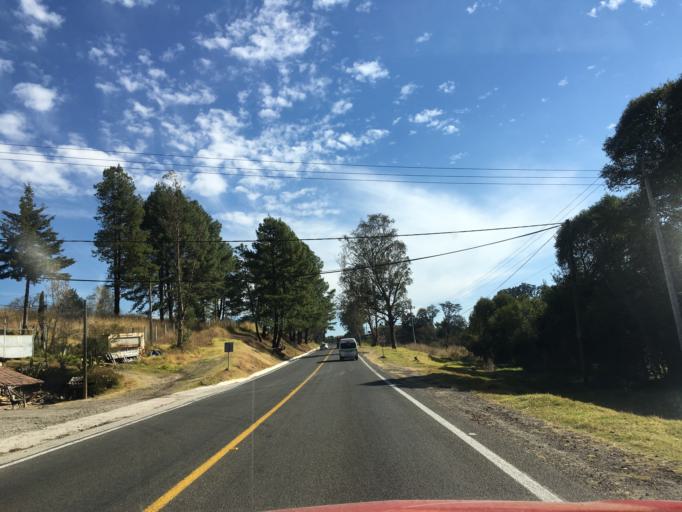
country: MX
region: Michoacan
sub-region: Hidalgo
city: San Lucas Huarirapeo (La Mesa de San Lucas)
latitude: 19.6653
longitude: -100.6805
